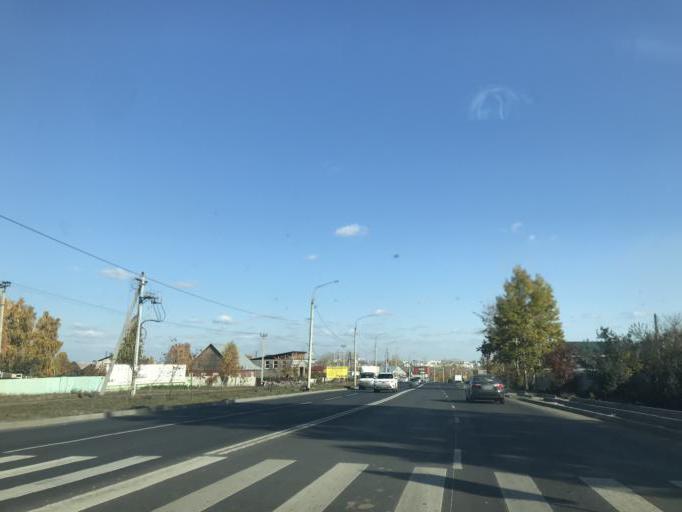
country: RU
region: Chelyabinsk
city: Roshchino
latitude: 55.2404
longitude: 61.3199
